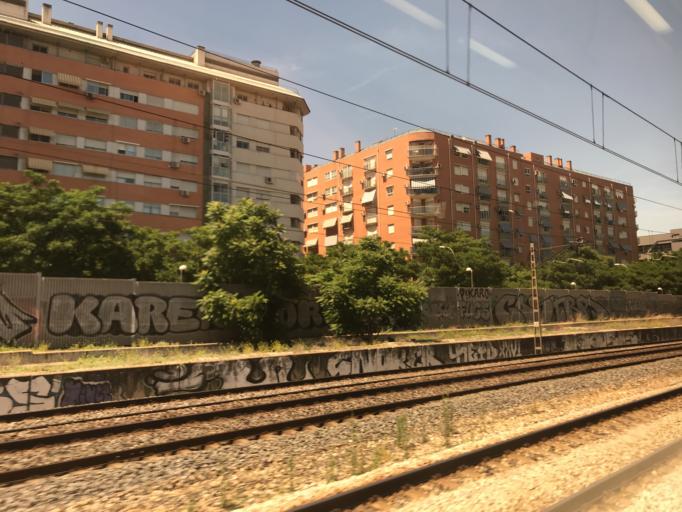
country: ES
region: Madrid
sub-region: Provincia de Madrid
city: Villaverde
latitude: 40.3574
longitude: -3.6830
